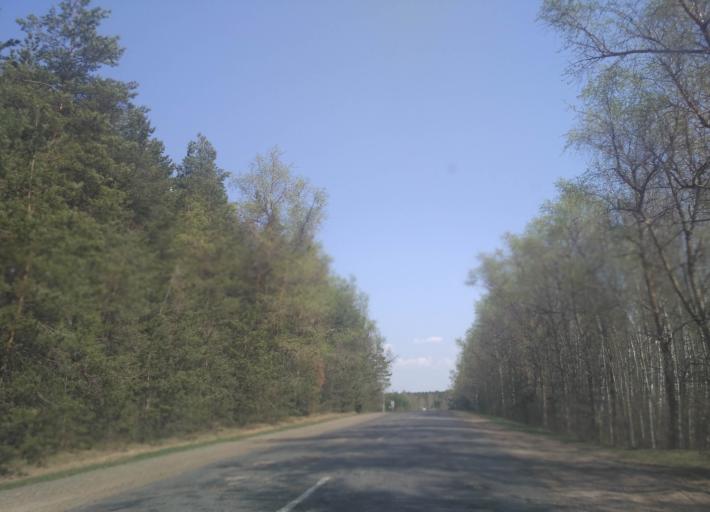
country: BY
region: Minsk
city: Loshnitsa
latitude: 54.4153
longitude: 28.6340
